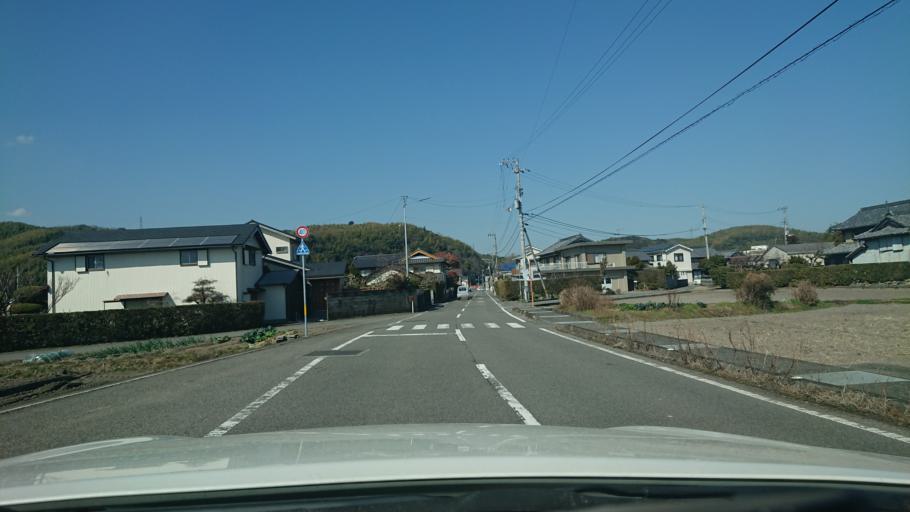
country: JP
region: Tokushima
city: Komatsushimacho
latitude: 33.9656
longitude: 134.6071
